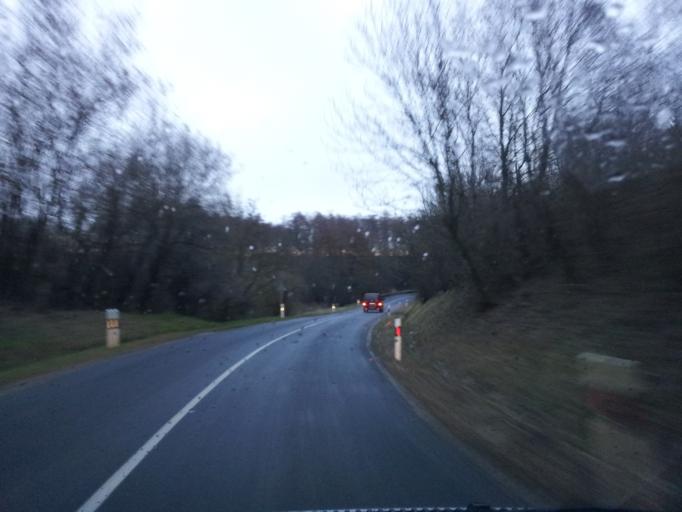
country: AT
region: Burgenland
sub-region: Politischer Bezirk Oberpullendorf
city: Lutzmannsburg
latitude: 47.4260
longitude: 16.6357
